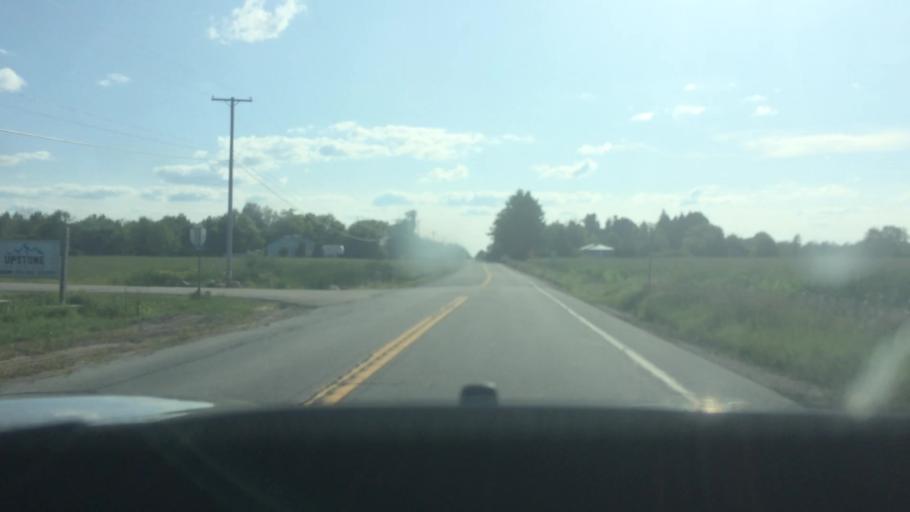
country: US
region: New York
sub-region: Franklin County
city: Malone
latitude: 44.7846
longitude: -74.4865
